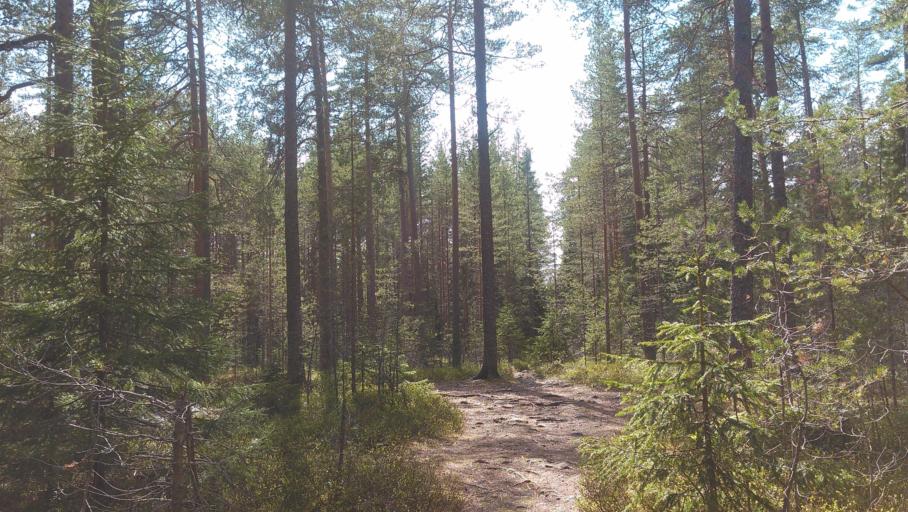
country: SE
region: Vaesterbotten
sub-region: Umea Kommun
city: Umea
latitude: 63.8372
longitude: 20.3001
